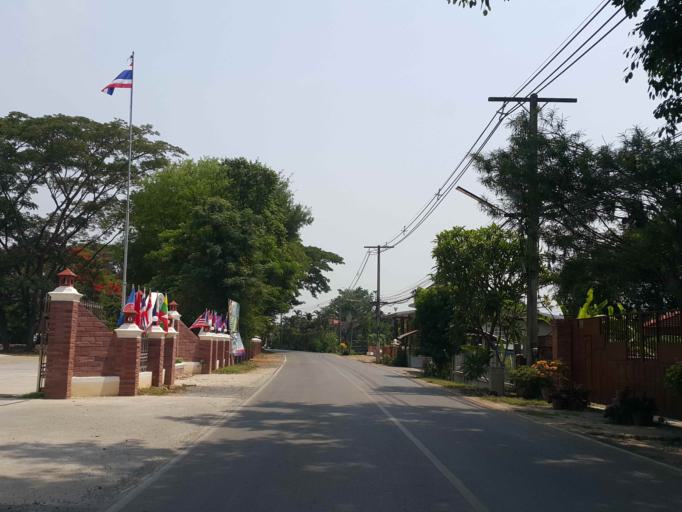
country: TH
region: Chiang Mai
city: San Sai
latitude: 18.8968
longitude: 98.9768
